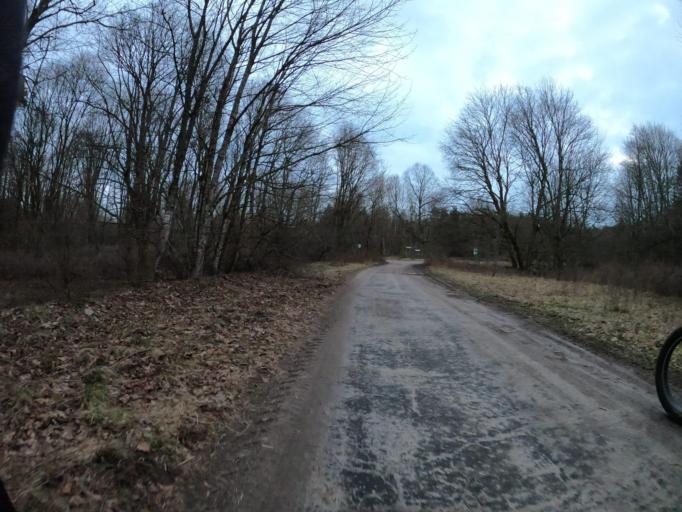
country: PL
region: West Pomeranian Voivodeship
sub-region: Powiat szczecinecki
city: Borne Sulinowo
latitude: 53.5439
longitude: 16.5847
